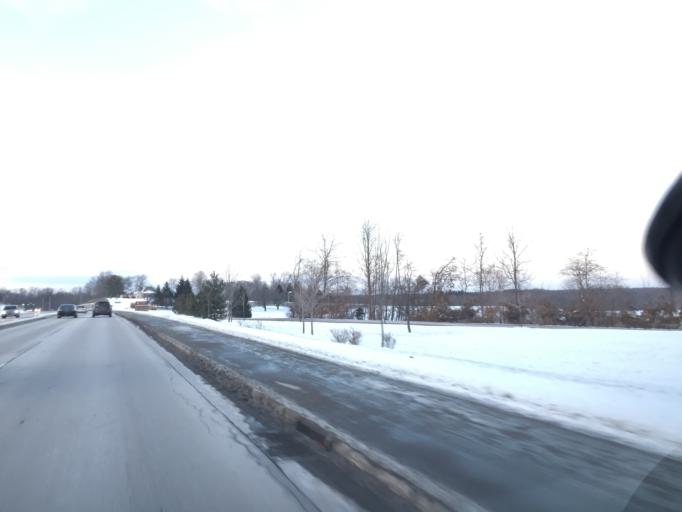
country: US
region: Indiana
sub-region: Monroe County
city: Bloomington
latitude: 39.1757
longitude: -86.5045
